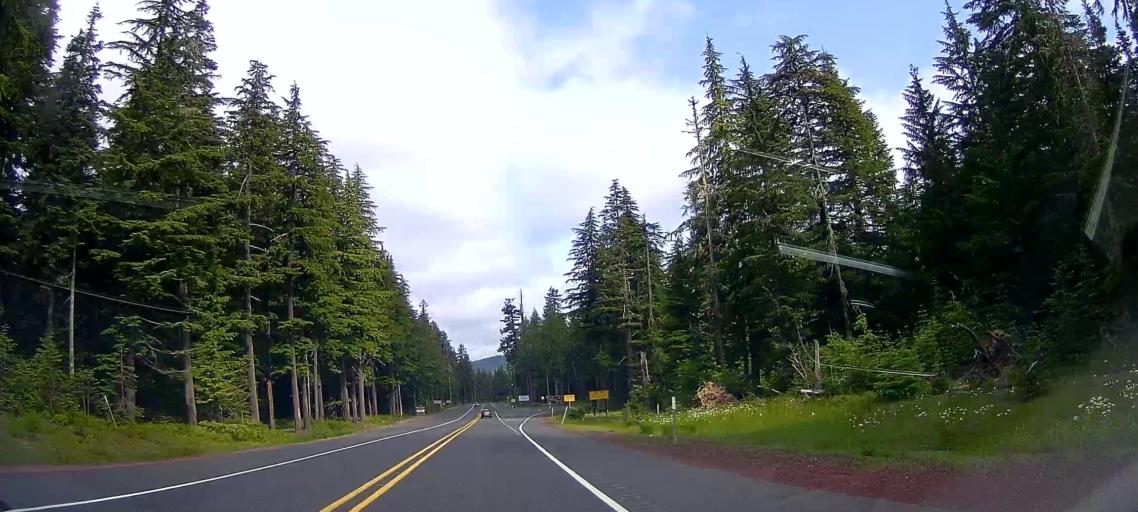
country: US
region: Oregon
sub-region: Clackamas County
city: Mount Hood Village
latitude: 45.2272
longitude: -121.6989
